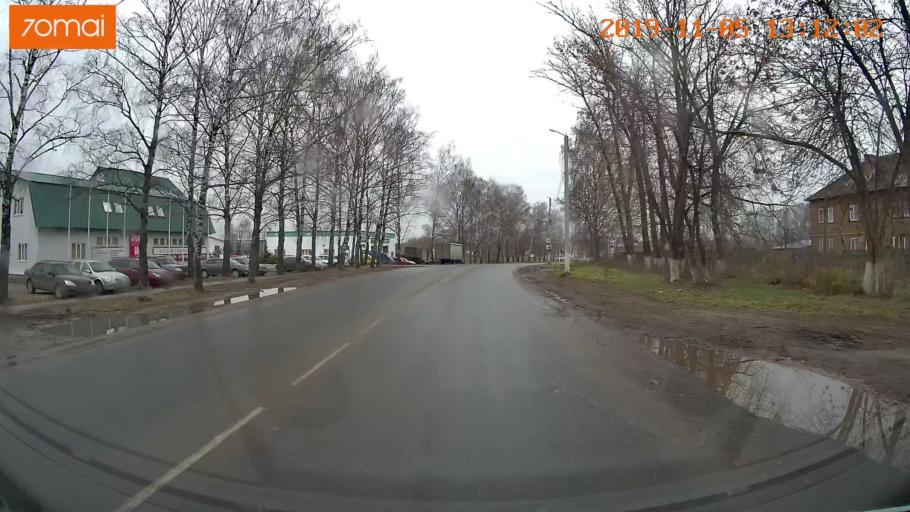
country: RU
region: Ivanovo
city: Shuya
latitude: 56.8577
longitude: 41.3479
